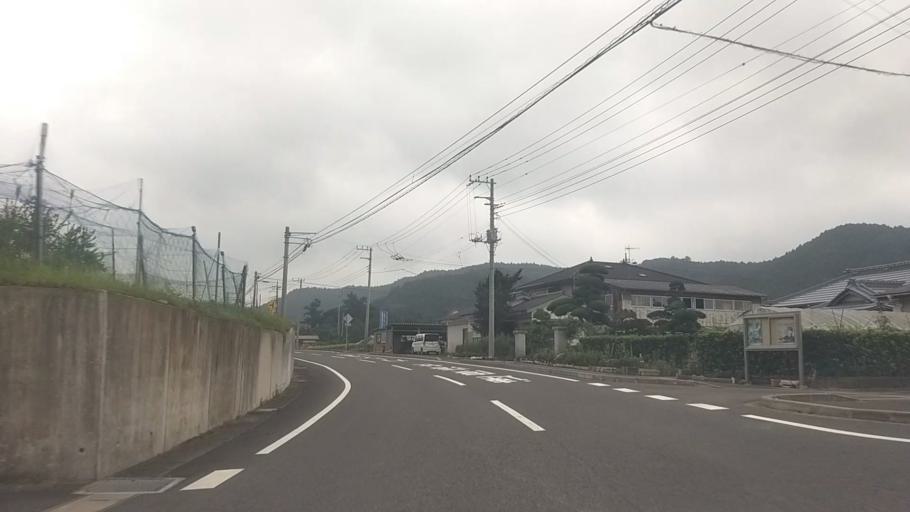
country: JP
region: Chiba
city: Kawaguchi
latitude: 35.2215
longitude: 140.1347
